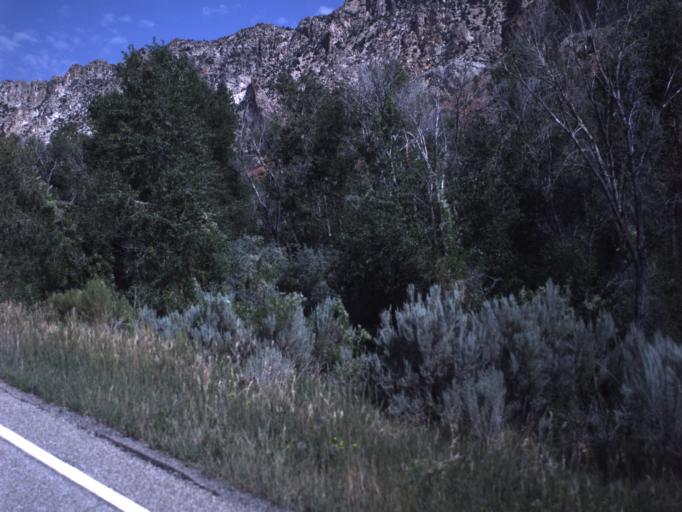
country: US
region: Utah
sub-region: Daggett County
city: Manila
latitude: 40.9209
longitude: -109.7017
